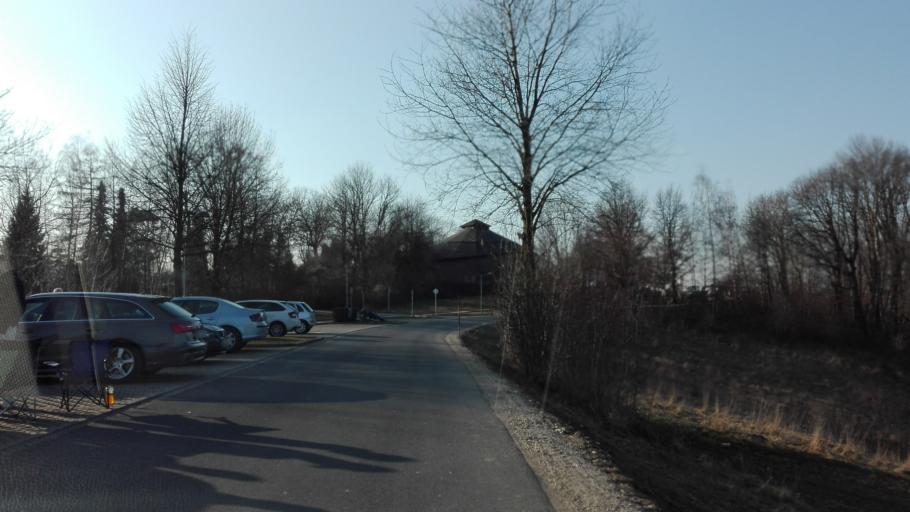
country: AT
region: Upper Austria
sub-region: Politischer Bezirk Linz-Land
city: Leonding
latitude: 48.2852
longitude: 14.2633
